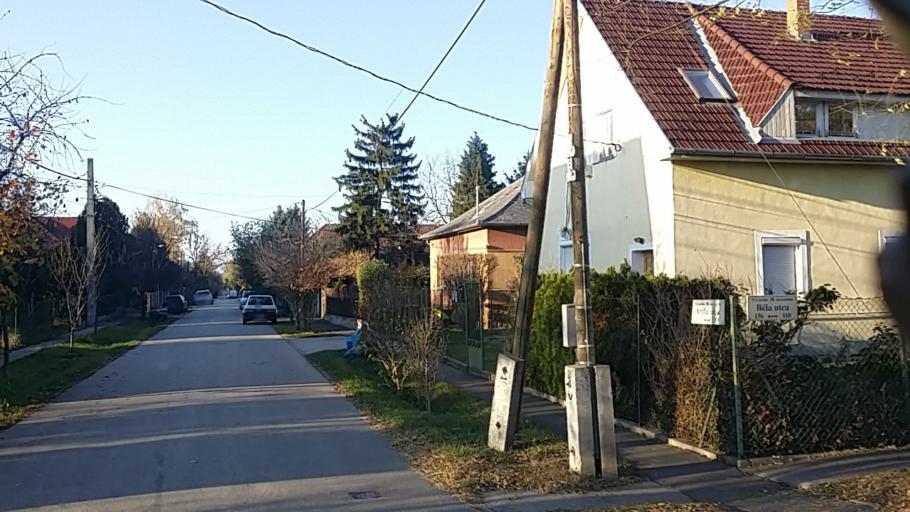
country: HU
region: Budapest
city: Budapest XVI. keruelet
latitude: 47.5274
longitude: 19.1769
